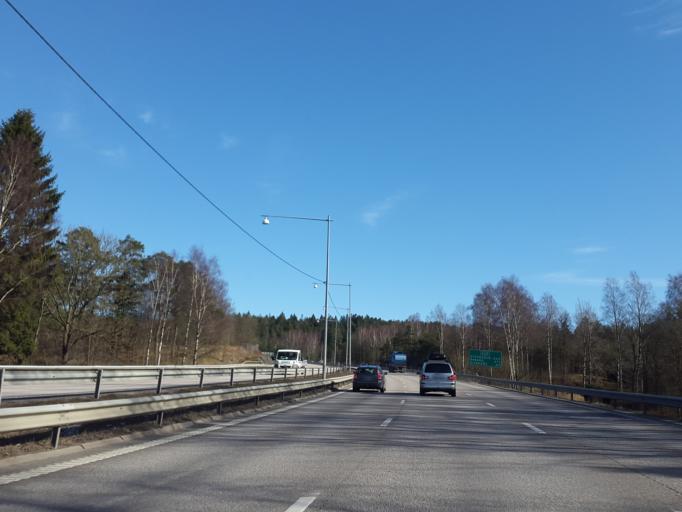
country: SE
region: Vaestra Goetaland
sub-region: Partille Kommun
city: Furulund
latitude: 57.7413
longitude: 12.1691
